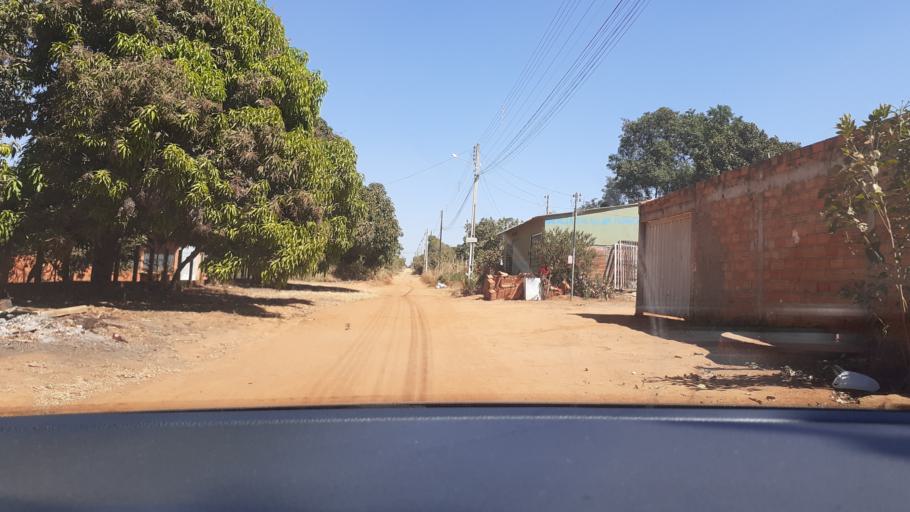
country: BR
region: Goias
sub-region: Aparecida De Goiania
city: Aparecida de Goiania
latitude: -16.8723
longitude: -49.2796
